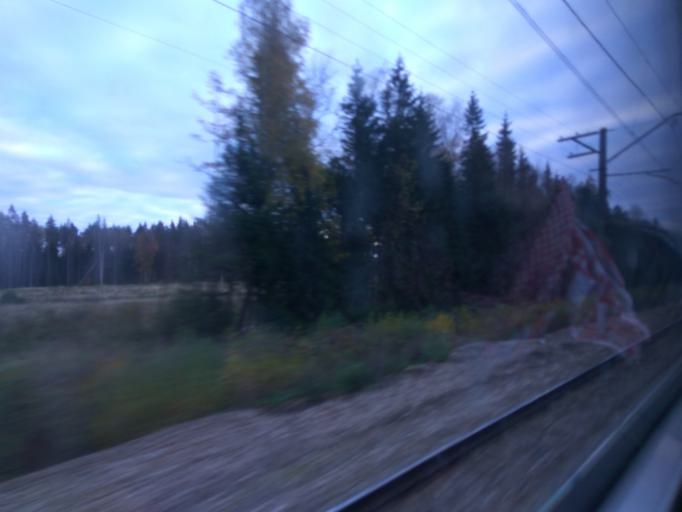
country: RU
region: Moskovskaya
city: Selyatino
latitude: 55.5047
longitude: 36.9467
